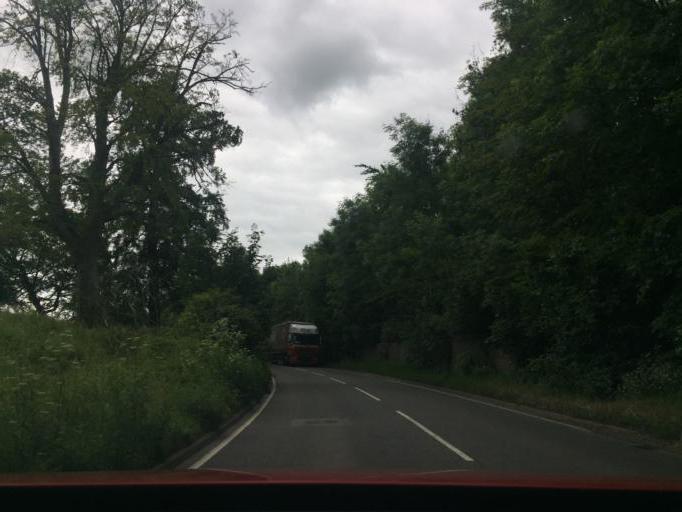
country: GB
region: England
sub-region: Luton
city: Luton
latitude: 51.8643
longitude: -0.3873
